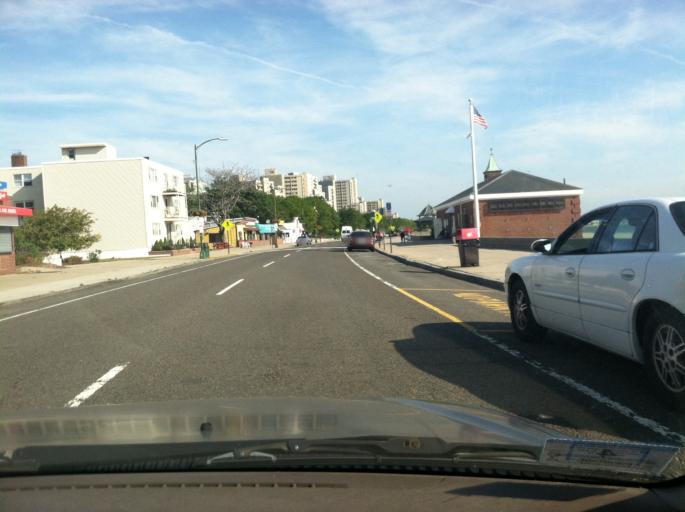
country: US
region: Massachusetts
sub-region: Suffolk County
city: Revere
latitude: 42.4007
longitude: -70.9903
